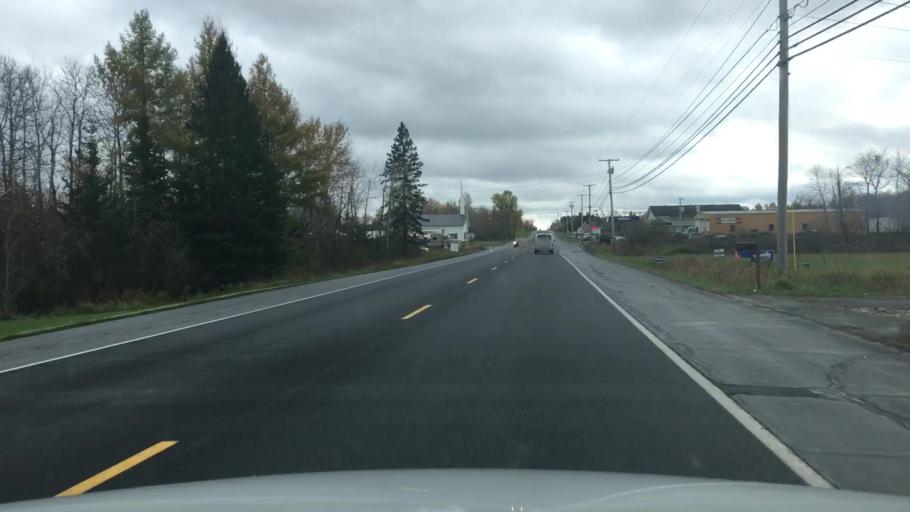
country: US
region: Maine
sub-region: Aroostook County
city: Houlton
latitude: 46.2434
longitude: -67.8408
